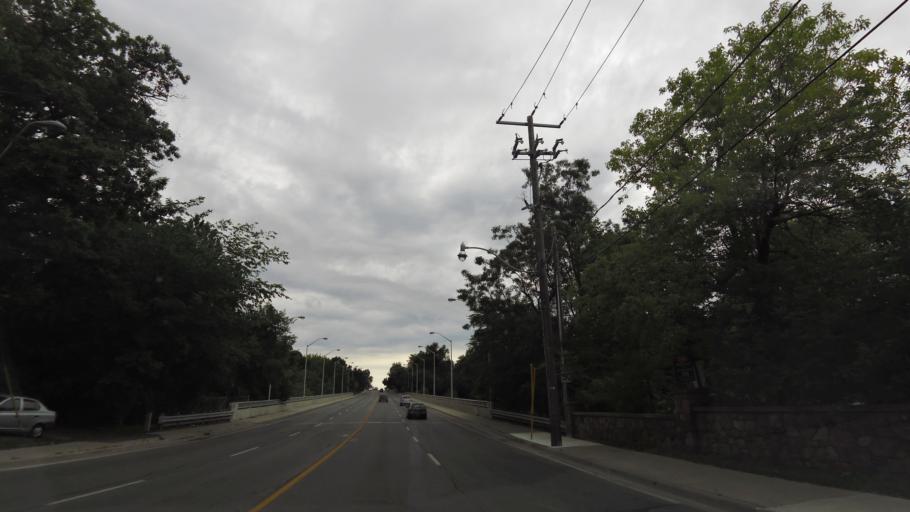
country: CA
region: Ontario
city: Toronto
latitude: 43.6893
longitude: -79.4208
